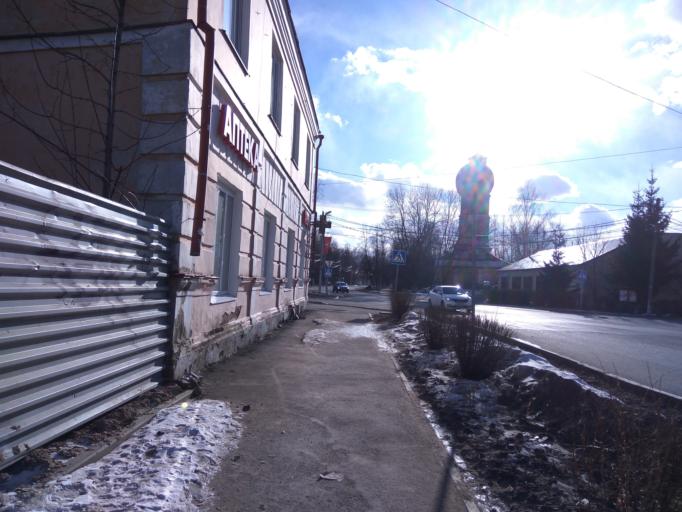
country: RU
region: Jaroslavl
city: Rostov
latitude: 57.1879
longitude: 39.4281
